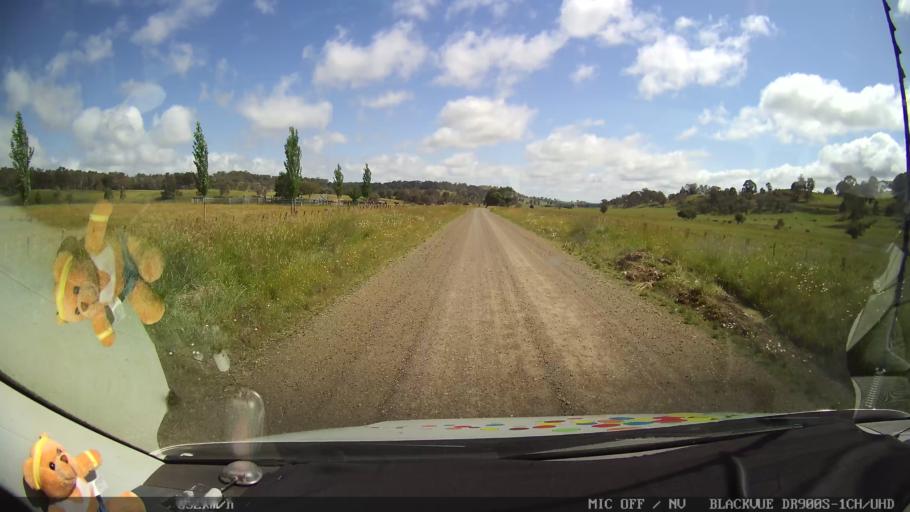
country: AU
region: New South Wales
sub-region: Glen Innes Severn
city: Glen Innes
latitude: -29.9718
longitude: 151.6993
